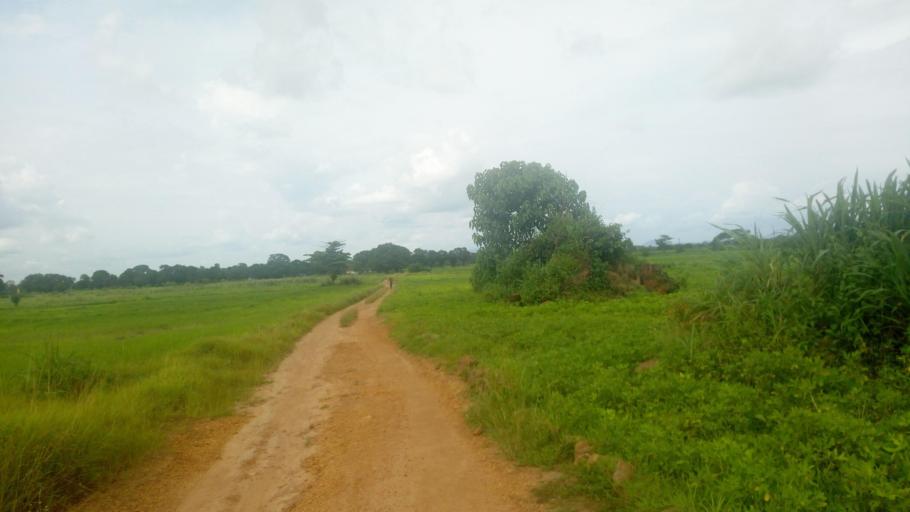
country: SL
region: Northern Province
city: Magburaka
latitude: 8.6743
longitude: -12.0160
